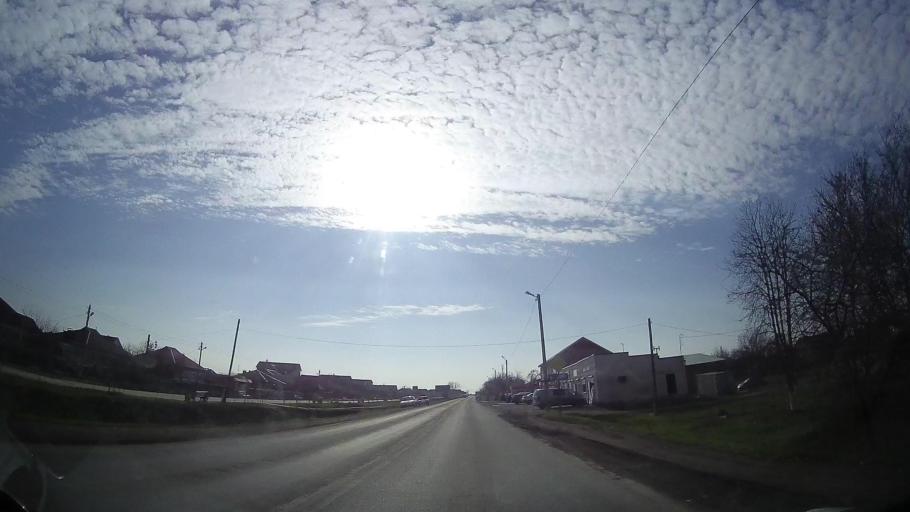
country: RU
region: Rostov
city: Tselina
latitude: 46.5366
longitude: 41.0513
